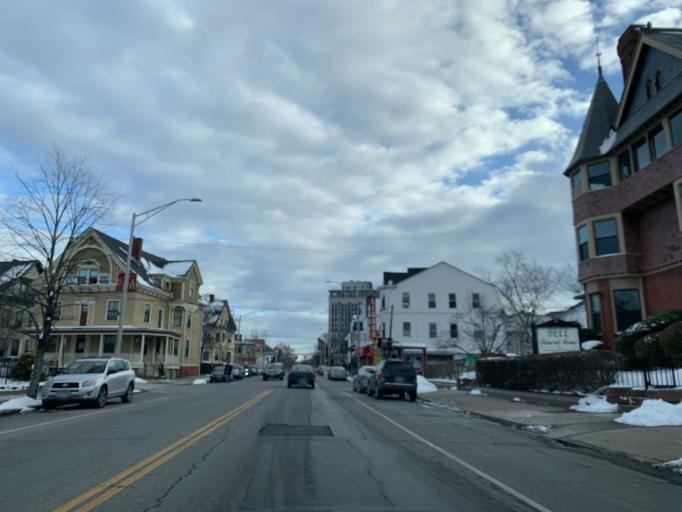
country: US
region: Rhode Island
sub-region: Providence County
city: Providence
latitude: 41.8090
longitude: -71.4208
